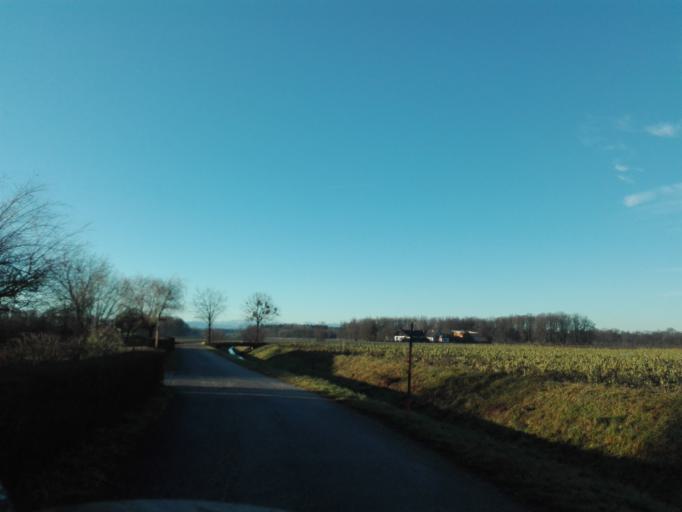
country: AT
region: Upper Austria
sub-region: Politischer Bezirk Perg
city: Perg
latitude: 48.2289
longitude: 14.6876
